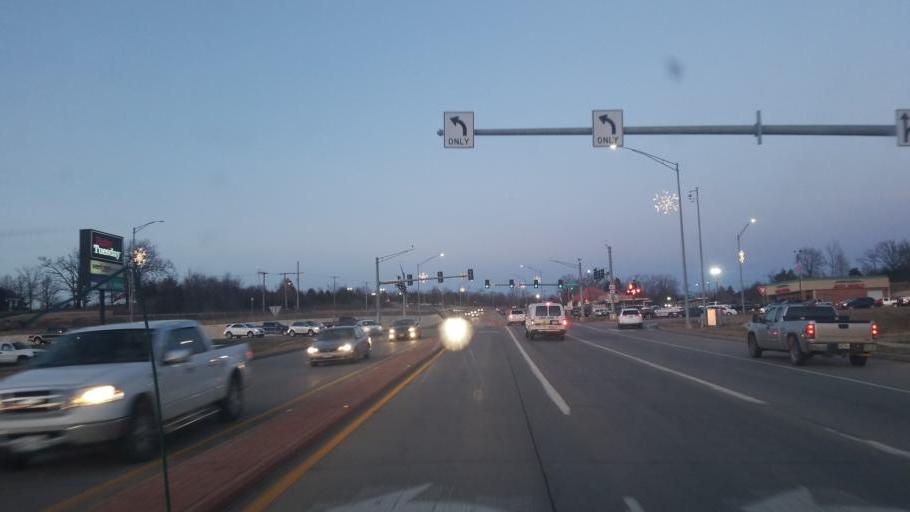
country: US
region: Missouri
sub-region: Howell County
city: West Plains
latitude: 36.7172
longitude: -91.8731
